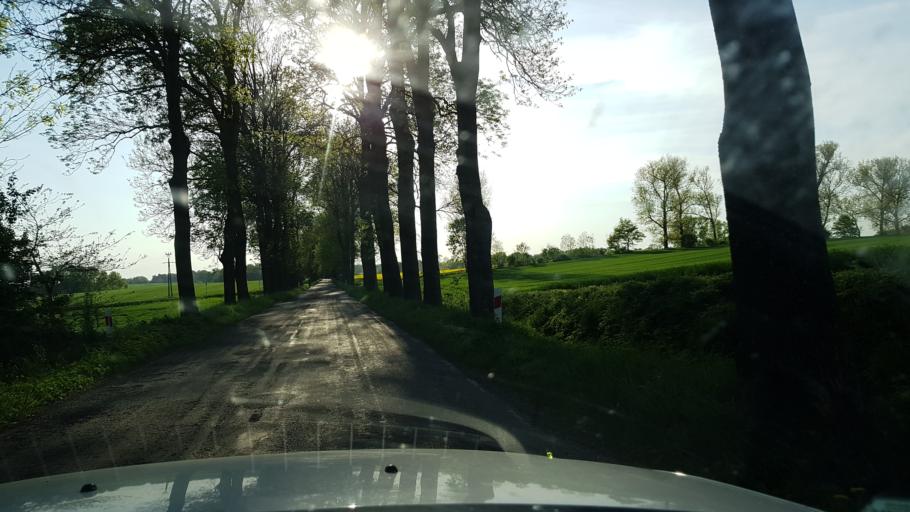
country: PL
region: West Pomeranian Voivodeship
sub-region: Powiat lobeski
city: Dobra
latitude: 53.5757
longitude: 15.2632
